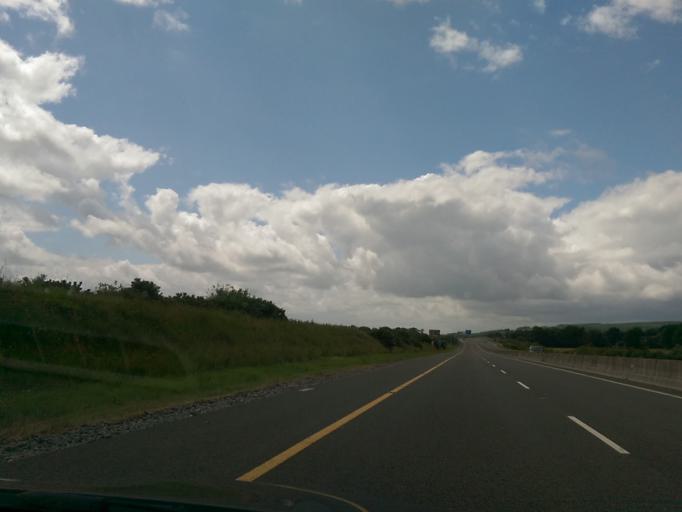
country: IE
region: Munster
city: Cahir
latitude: 52.3612
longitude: -7.9871
